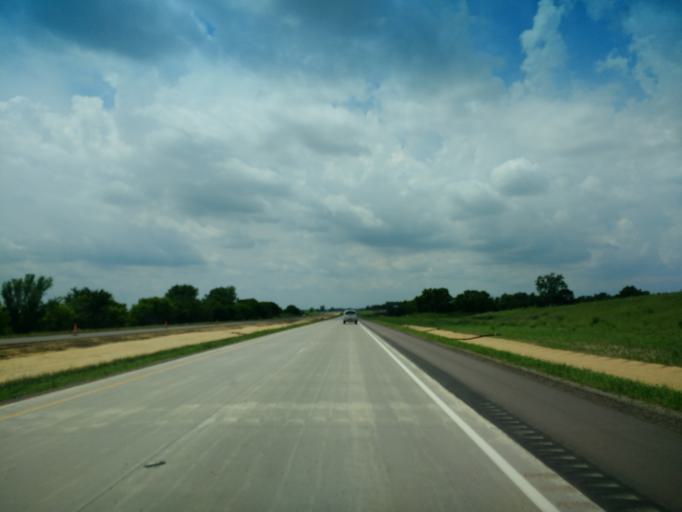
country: US
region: Minnesota
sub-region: Cottonwood County
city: Windom
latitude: 43.8994
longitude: -95.0694
